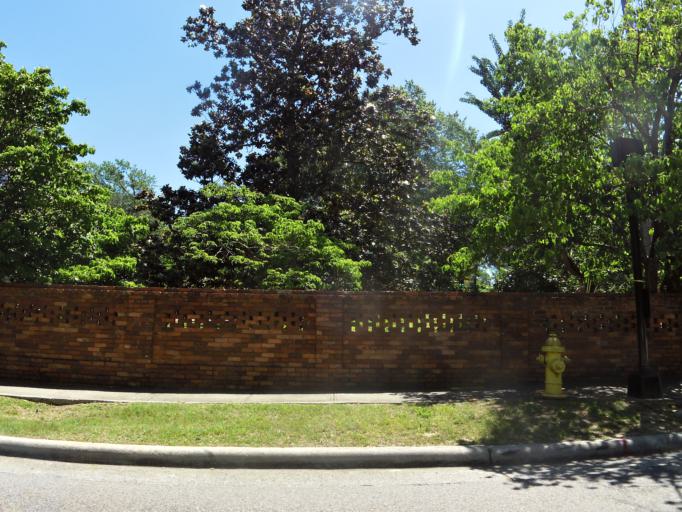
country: US
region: Georgia
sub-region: Richmond County
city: Augusta
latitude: 33.4790
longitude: -82.0312
